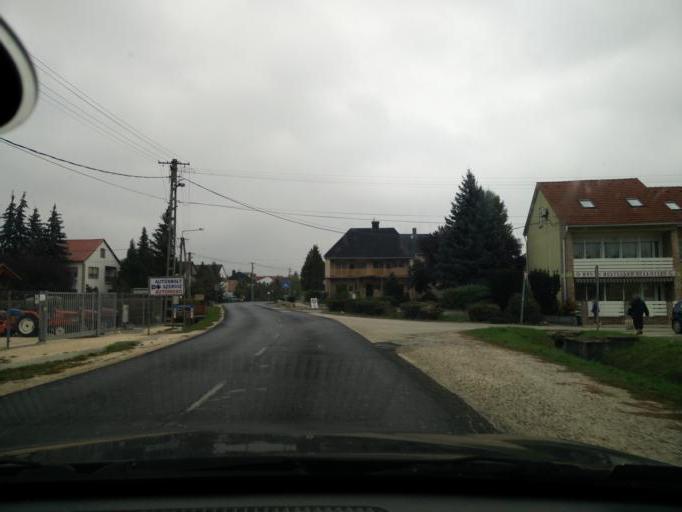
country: HU
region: Komarom-Esztergom
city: Tarjan
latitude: 47.6082
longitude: 18.5040
